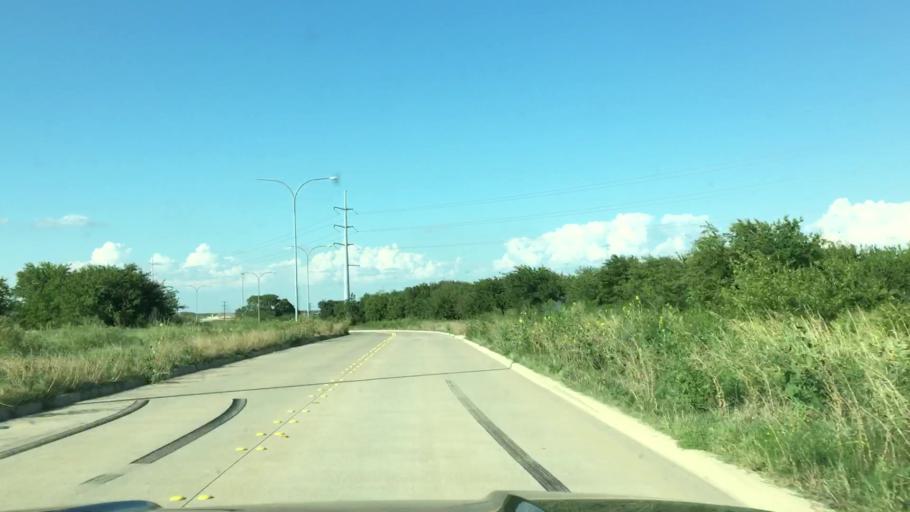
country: US
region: Texas
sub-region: Tarrant County
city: Haslet
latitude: 33.0087
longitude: -97.3568
